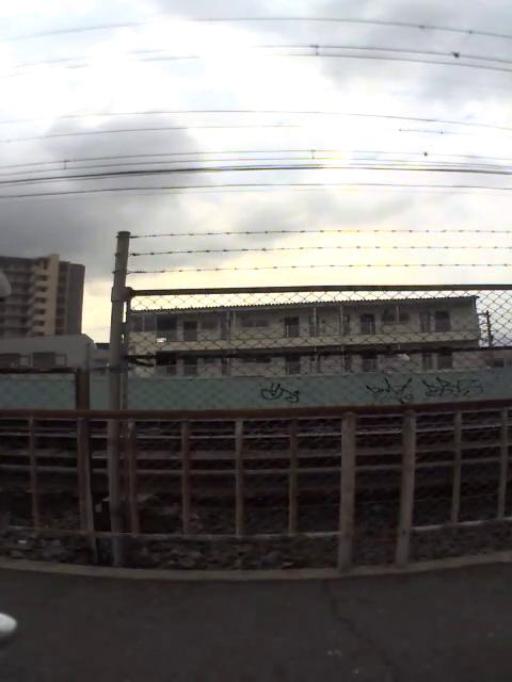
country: JP
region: Osaka
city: Hirakata
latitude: 34.8286
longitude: 135.6533
